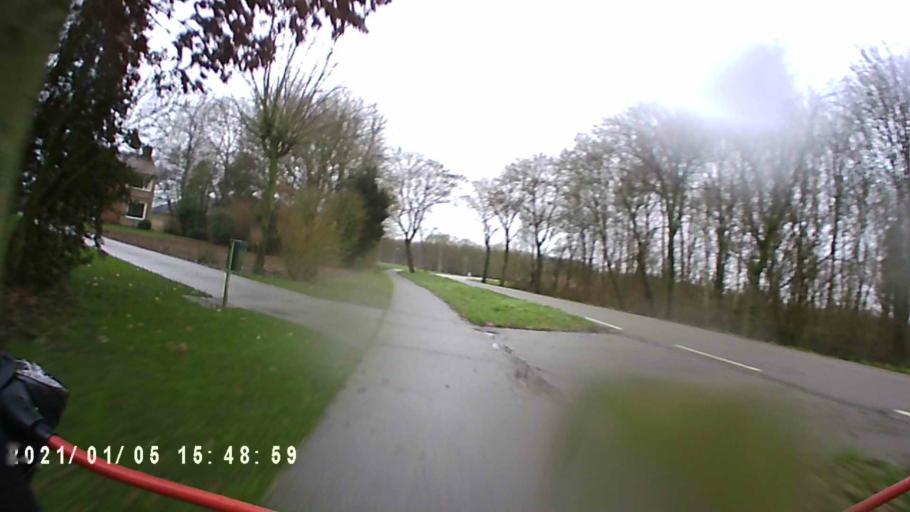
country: NL
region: Groningen
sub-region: Gemeente  Oldambt
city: Winschoten
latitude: 53.1988
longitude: 7.1103
